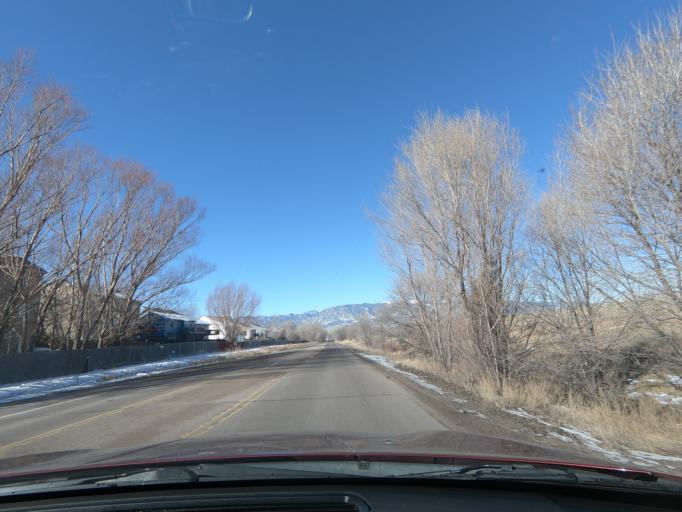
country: US
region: Colorado
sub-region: El Paso County
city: Security-Widefield
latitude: 38.7375
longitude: -104.6956
